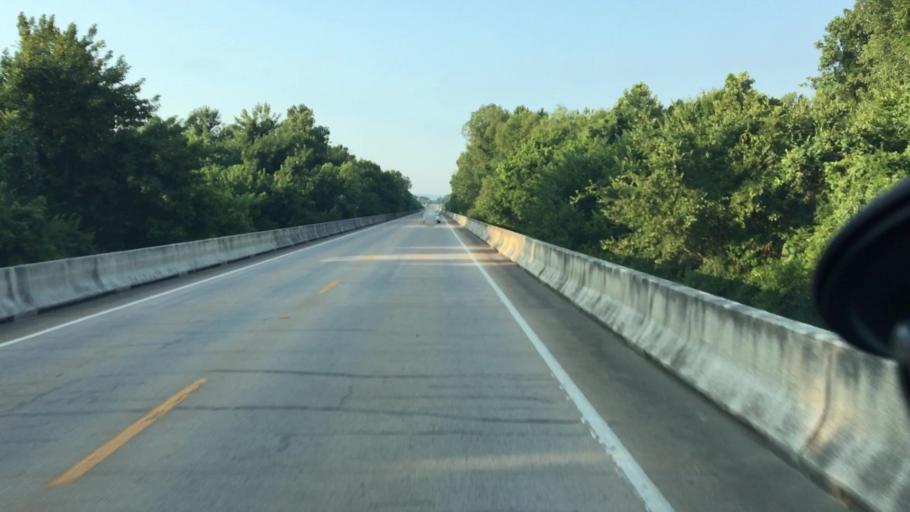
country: US
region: Arkansas
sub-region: Johnson County
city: Clarksville
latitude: 35.4035
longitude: -93.5314
